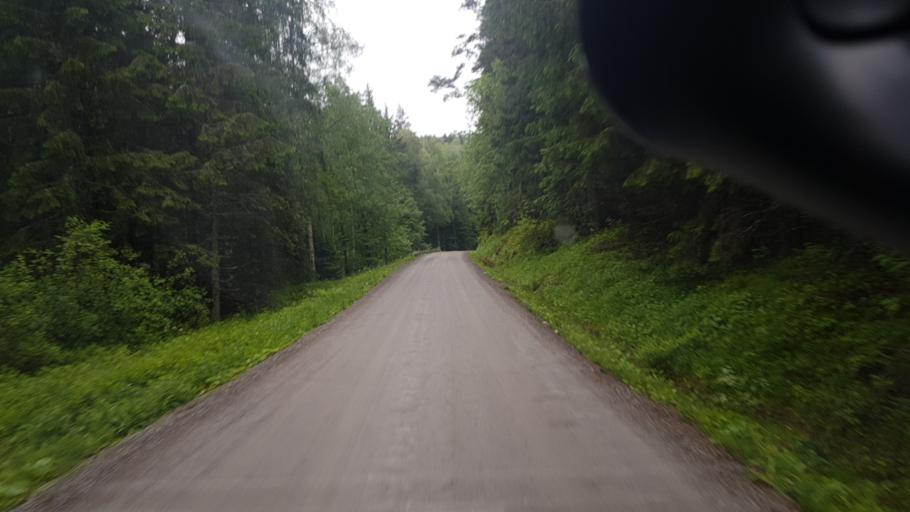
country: NO
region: Ostfold
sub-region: Romskog
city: Romskog
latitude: 59.6996
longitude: 11.9461
